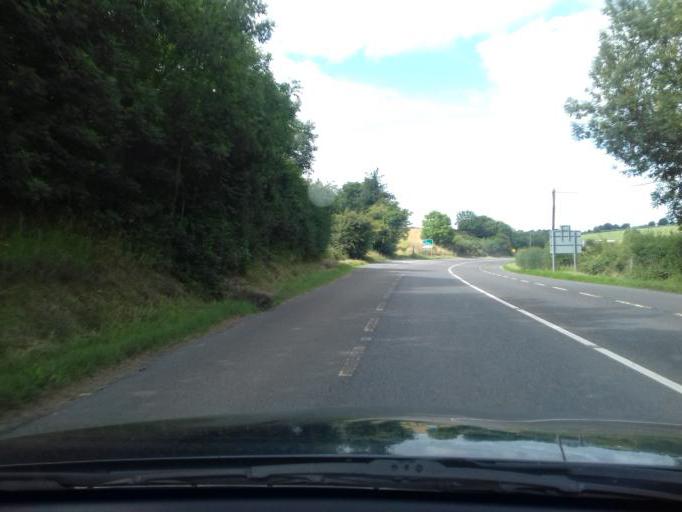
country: IE
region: Leinster
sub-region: Wicklow
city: Baltinglass
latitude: 53.0098
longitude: -6.6420
